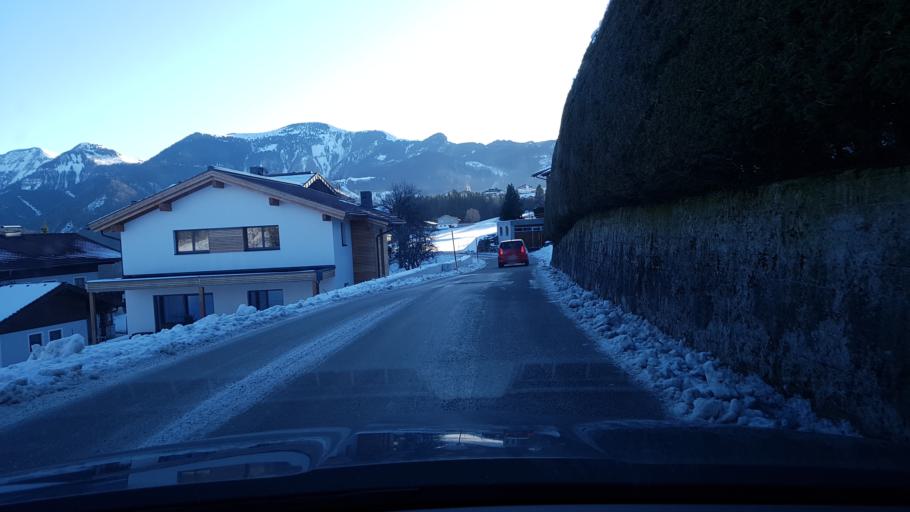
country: AT
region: Salzburg
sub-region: Politischer Bezirk Hallein
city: Kuchl
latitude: 47.6569
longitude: 13.1927
